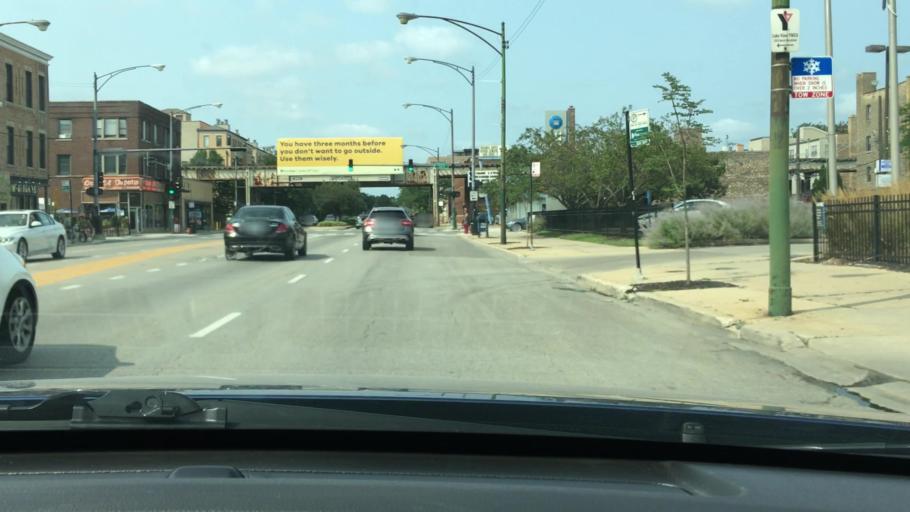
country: US
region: Illinois
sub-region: Cook County
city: Lincolnwood
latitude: 41.9427
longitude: -87.6686
